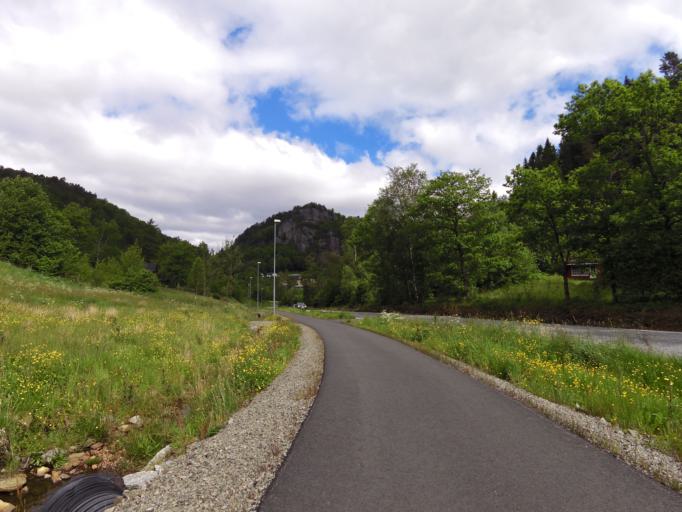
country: NO
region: Vest-Agder
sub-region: Flekkefjord
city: Flekkefjord
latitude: 58.2656
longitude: 6.8086
